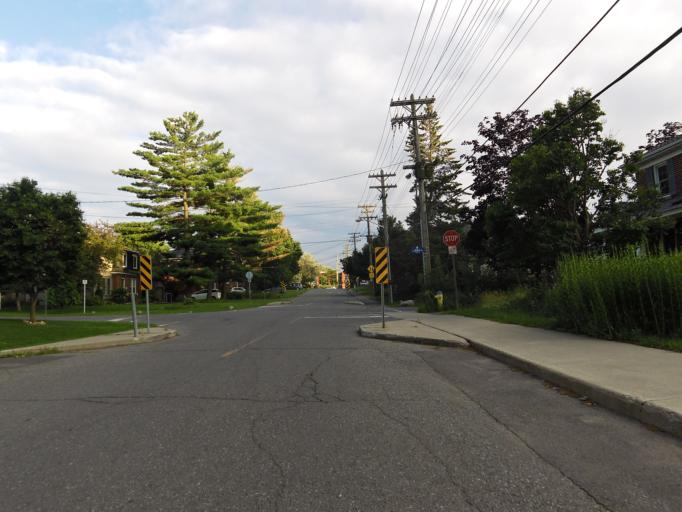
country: CA
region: Ontario
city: Ottawa
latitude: 45.3964
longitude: -75.7487
